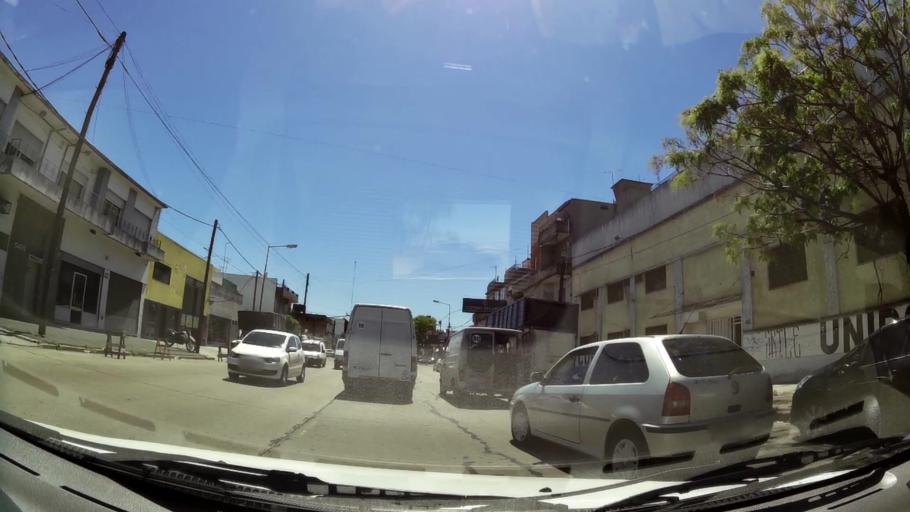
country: AR
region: Buenos Aires
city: Caseros
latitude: -34.5838
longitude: -58.5570
